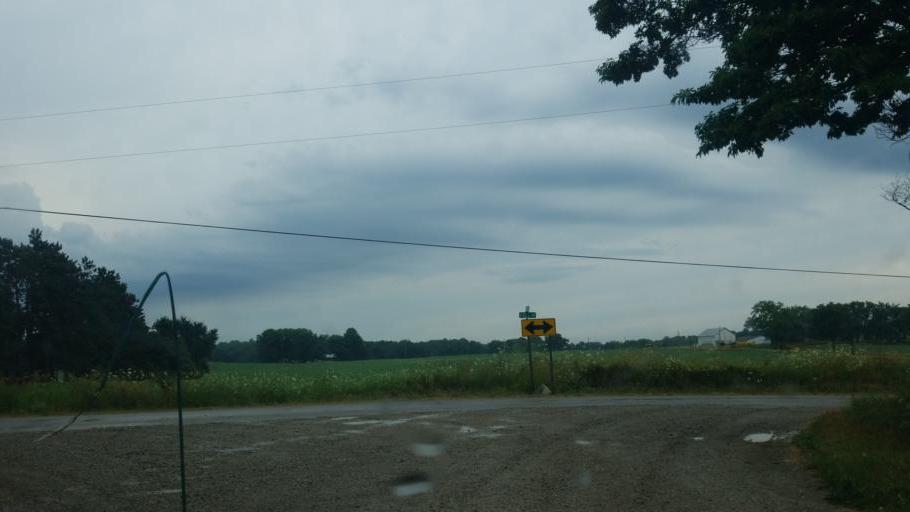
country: US
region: Indiana
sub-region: Steuben County
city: Hamilton
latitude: 41.5149
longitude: -84.9334
